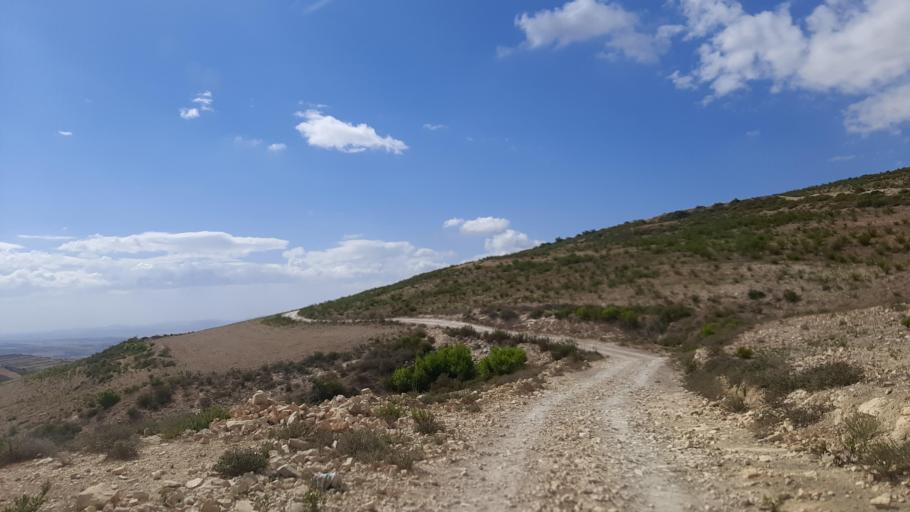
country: TN
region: Zaghwan
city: Zaghouan
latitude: 36.5084
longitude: 10.1839
